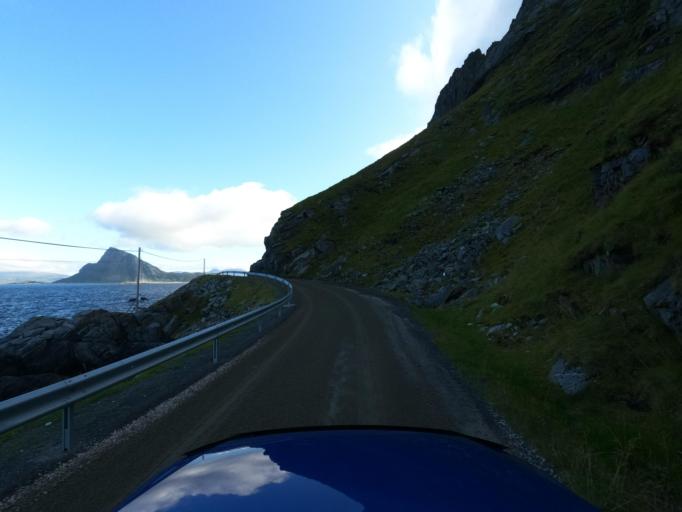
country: NO
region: Nordland
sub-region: Vestvagoy
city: Gravdal
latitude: 68.1642
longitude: 13.3869
